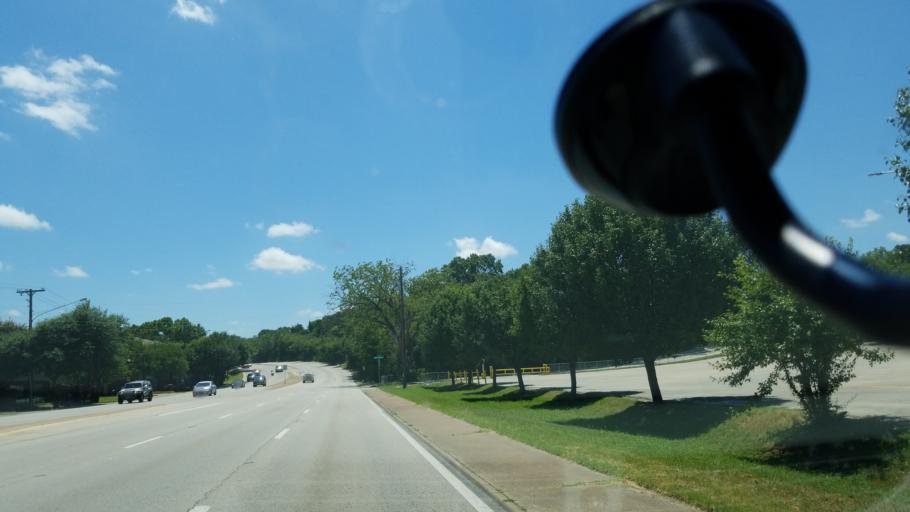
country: US
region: Texas
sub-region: Dallas County
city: Cockrell Hill
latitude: 32.6853
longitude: -96.8195
